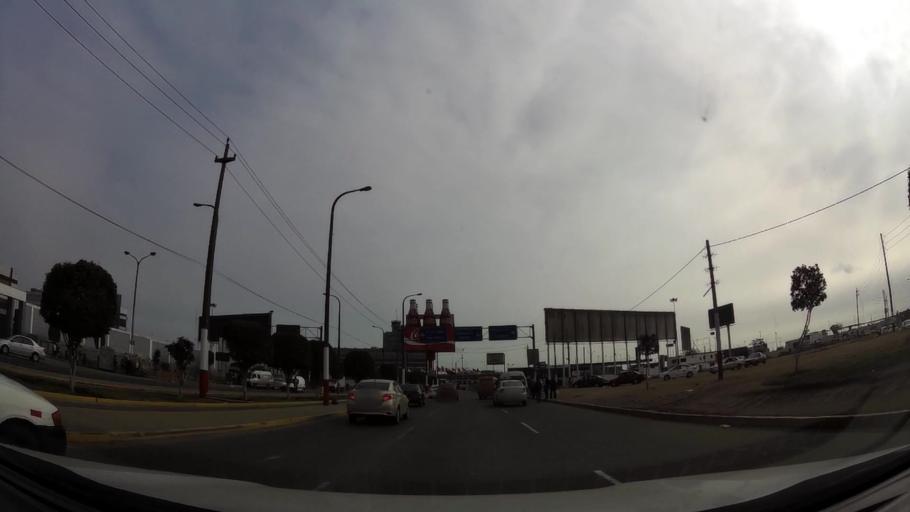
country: PE
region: Callao
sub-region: Callao
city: Callao
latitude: -12.0212
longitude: -77.1047
